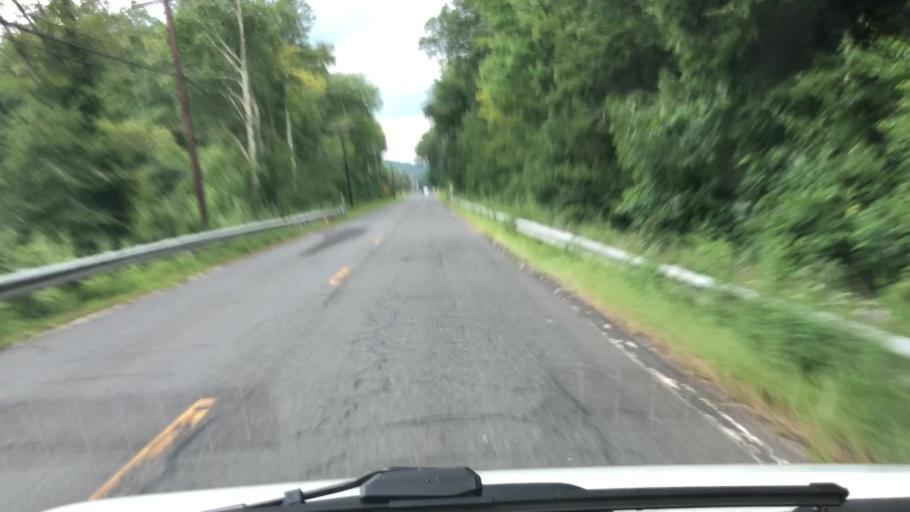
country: US
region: Massachusetts
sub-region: Franklin County
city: South Deerfield
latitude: 42.4862
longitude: -72.6214
